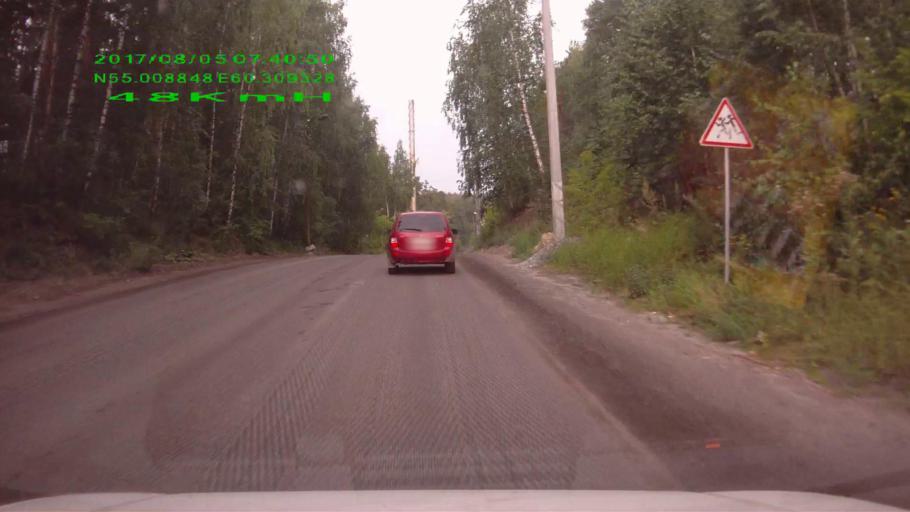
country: RU
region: Chelyabinsk
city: Chebarkul'
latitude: 55.0089
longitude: 60.3093
